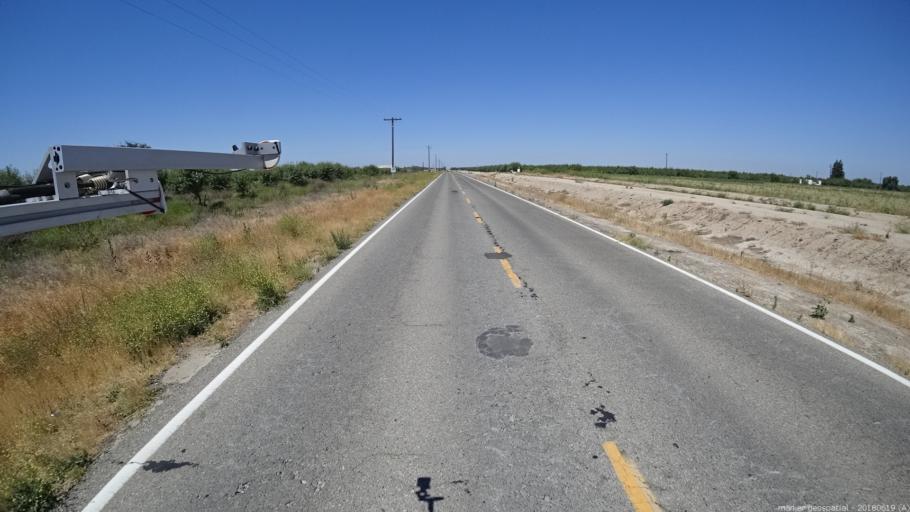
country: US
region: California
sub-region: Madera County
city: Parkwood
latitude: 36.8512
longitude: -120.1449
